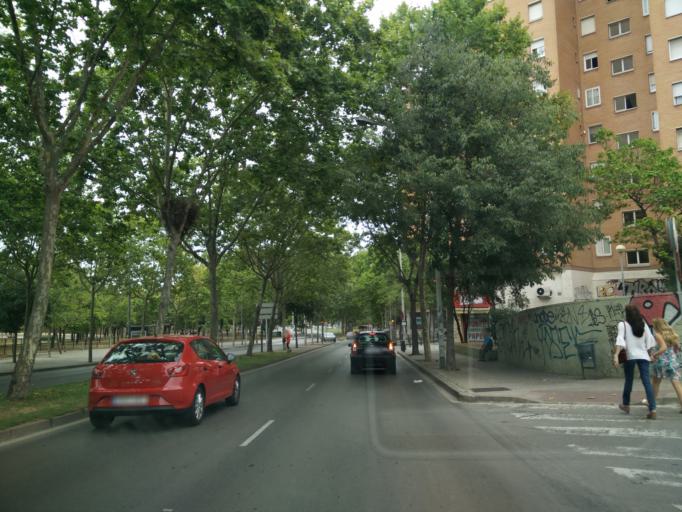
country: ES
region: Catalonia
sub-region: Provincia de Barcelona
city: Llefia
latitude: 41.4532
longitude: 2.2293
